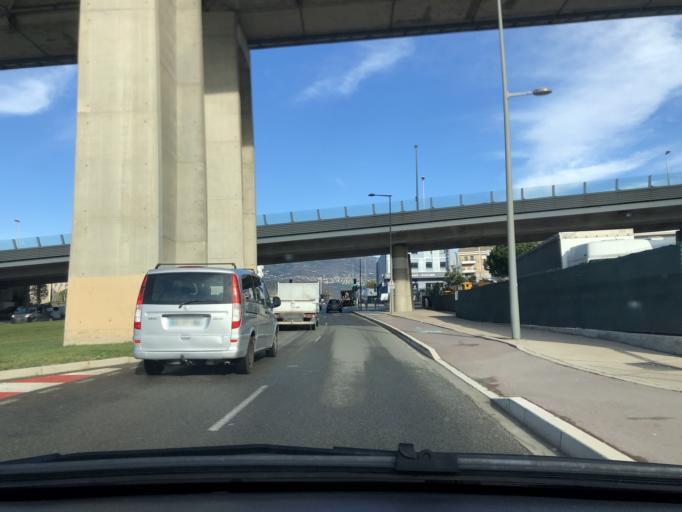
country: FR
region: Provence-Alpes-Cote d'Azur
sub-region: Departement des Alpes-Maritimes
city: Saint-Laurent-du-Var
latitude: 43.7090
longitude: 7.1957
